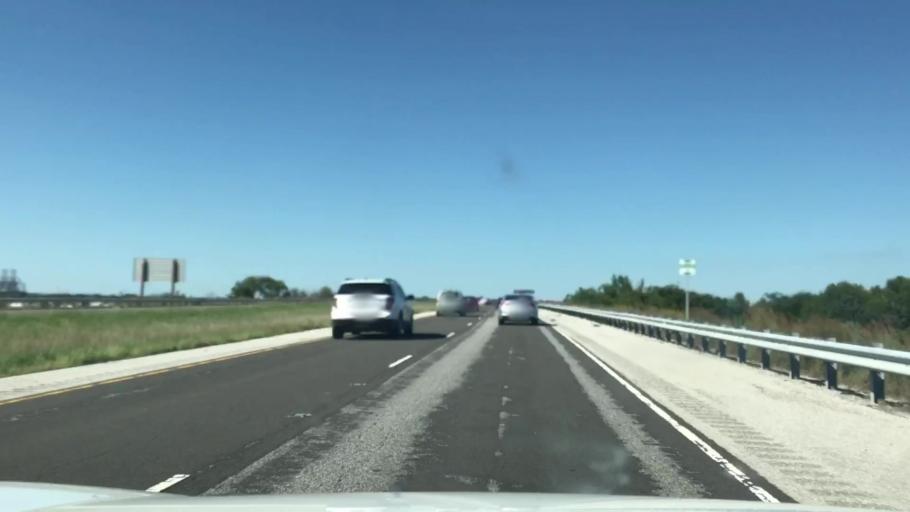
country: US
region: Illinois
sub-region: Madison County
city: South Roxana
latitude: 38.8155
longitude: -90.0422
